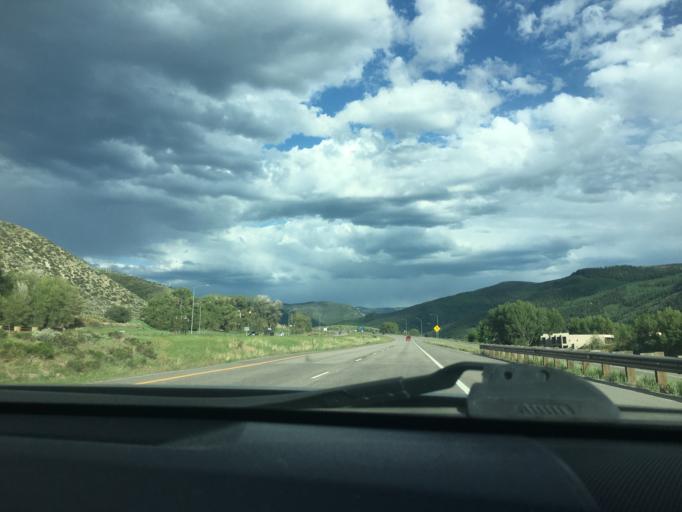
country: US
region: Colorado
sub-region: Eagle County
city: Avon
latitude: 39.6369
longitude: -106.5210
